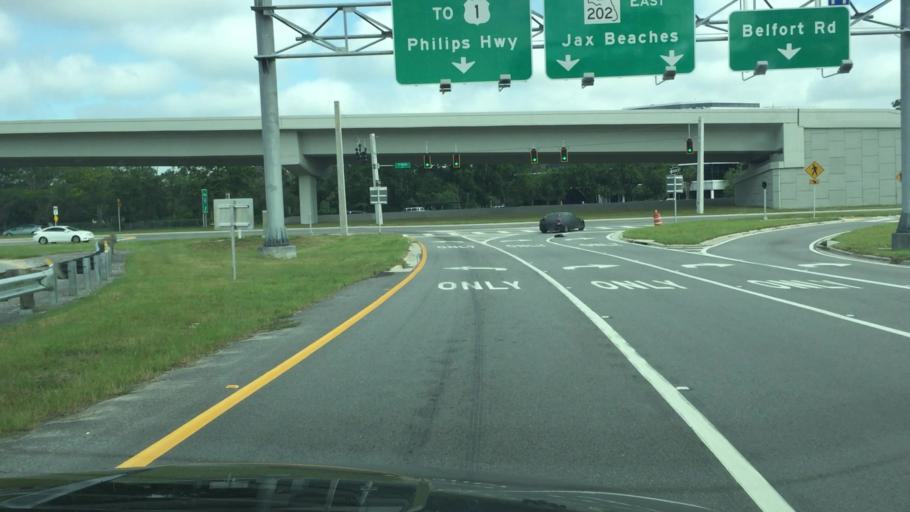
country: US
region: Florida
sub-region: Duval County
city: Jacksonville
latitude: 30.2488
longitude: -81.5913
